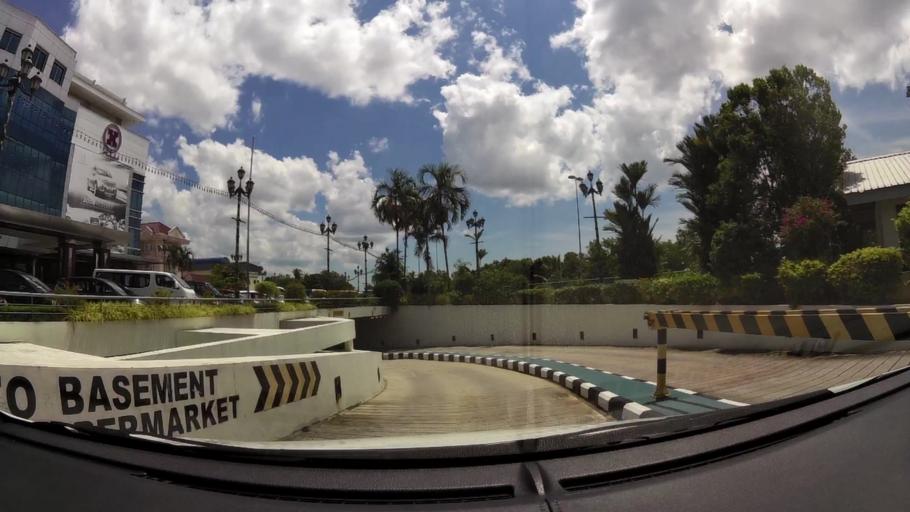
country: BN
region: Brunei and Muara
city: Bandar Seri Begawan
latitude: 4.9477
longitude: 114.9608
